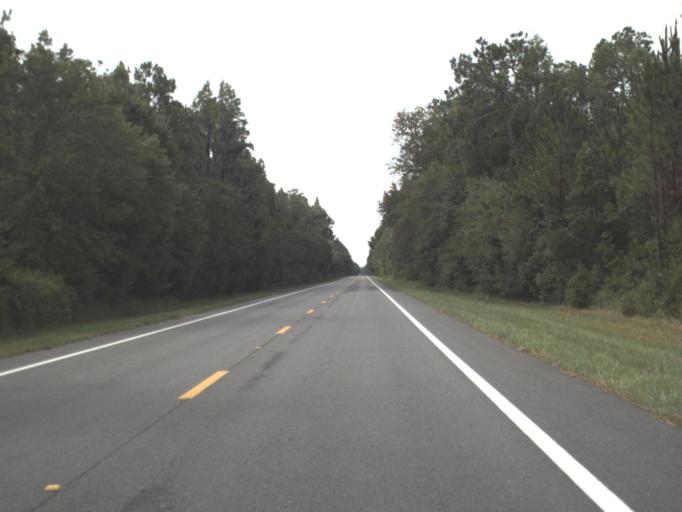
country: US
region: Florida
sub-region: Hamilton County
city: Jasper
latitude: 30.5765
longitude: -82.6795
